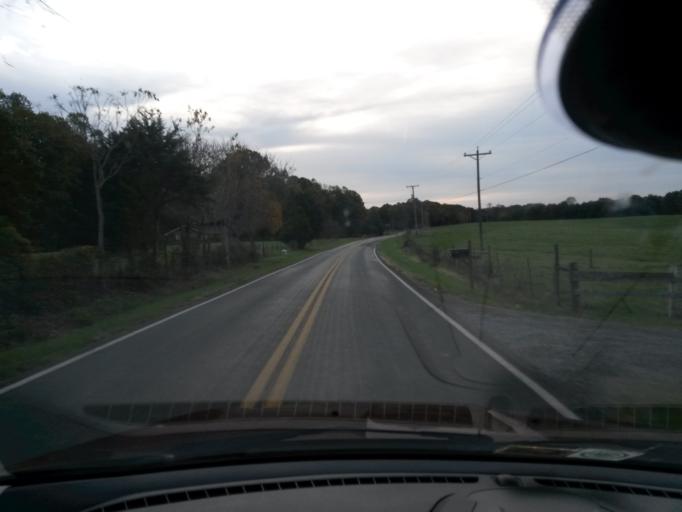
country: US
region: Virginia
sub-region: Franklin County
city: North Shore
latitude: 37.1508
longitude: -79.7937
